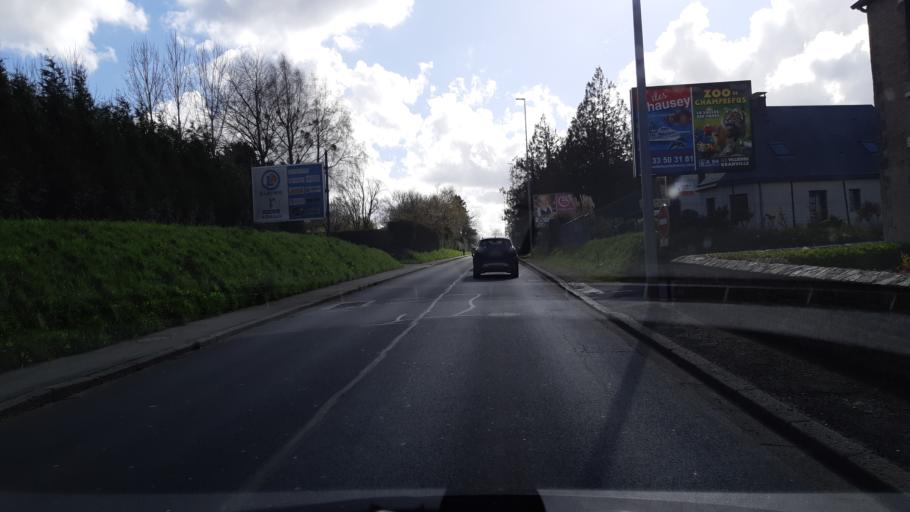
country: FR
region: Lower Normandy
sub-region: Departement de la Manche
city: Agneaux
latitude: 49.1046
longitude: -1.1115
